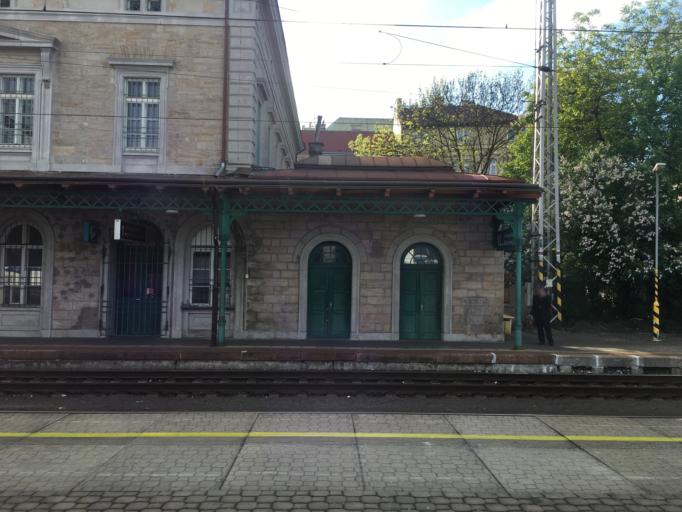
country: CZ
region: Ustecky
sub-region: Okres Decin
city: Decin
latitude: 50.7739
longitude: 14.2014
